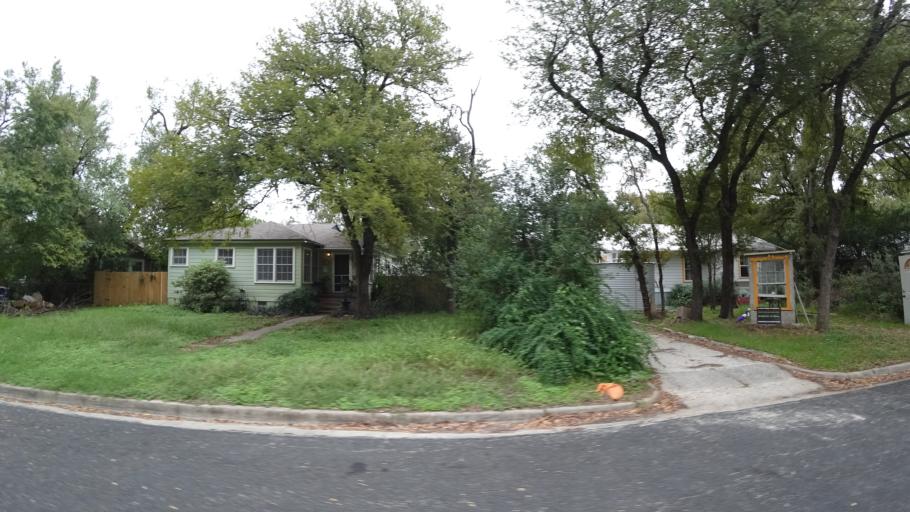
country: US
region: Texas
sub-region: Travis County
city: Austin
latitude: 30.2868
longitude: -97.7182
